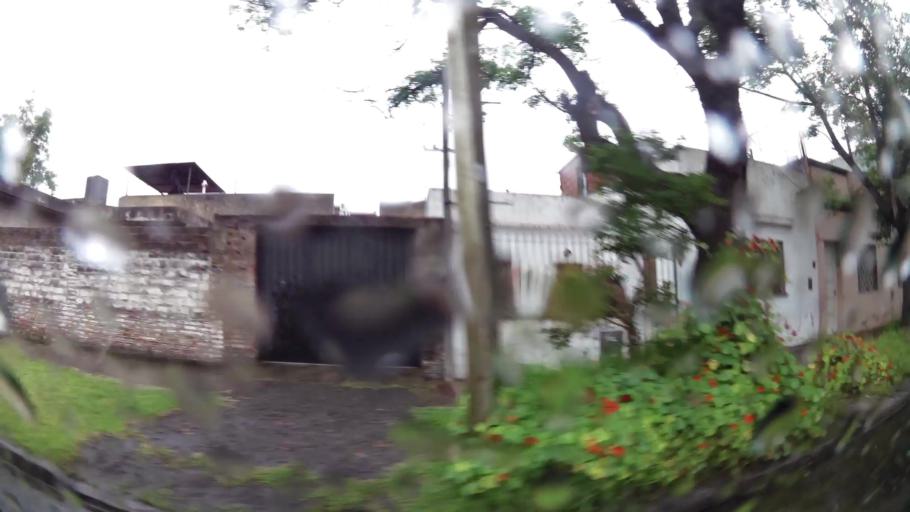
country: AR
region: Buenos Aires
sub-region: Partido de Lanus
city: Lanus
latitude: -34.7038
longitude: -58.4127
